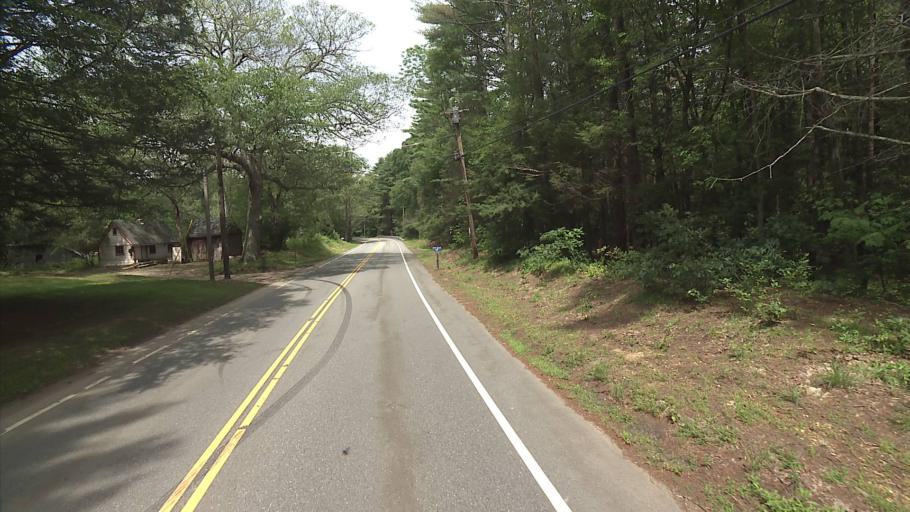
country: US
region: Massachusetts
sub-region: Hampden County
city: Holland
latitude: 41.9445
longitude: -72.1036
